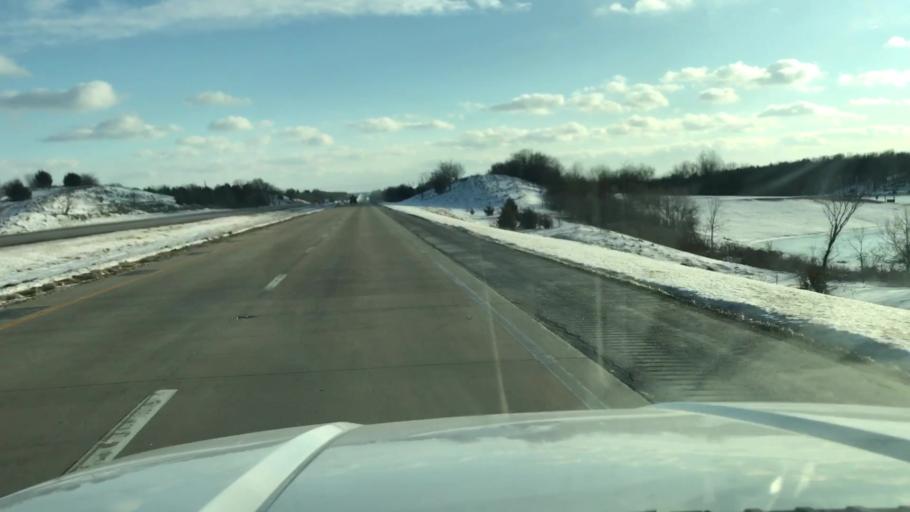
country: US
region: Missouri
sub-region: Andrew County
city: Savannah
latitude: 39.9517
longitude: -94.8603
